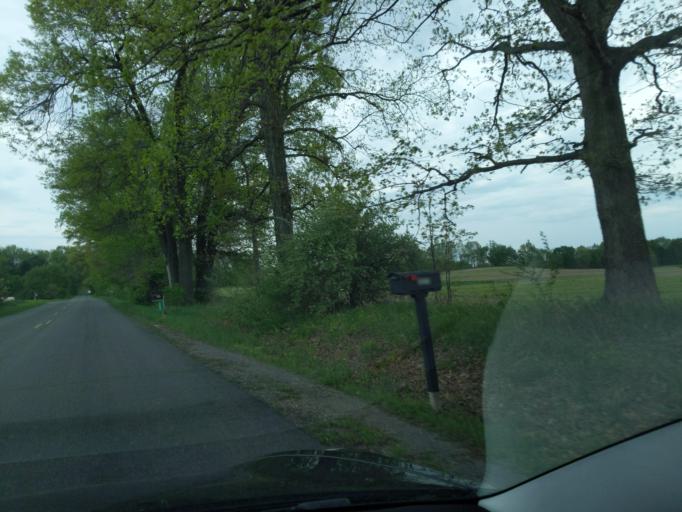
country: US
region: Michigan
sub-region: Ingham County
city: Stockbridge
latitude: 42.4423
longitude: -84.2146
